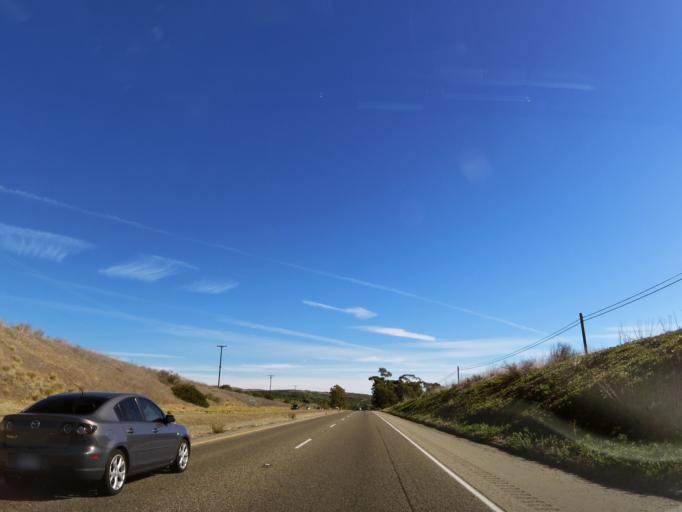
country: US
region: California
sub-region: Santa Barbara County
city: Isla Vista
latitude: 34.4580
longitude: -119.9858
